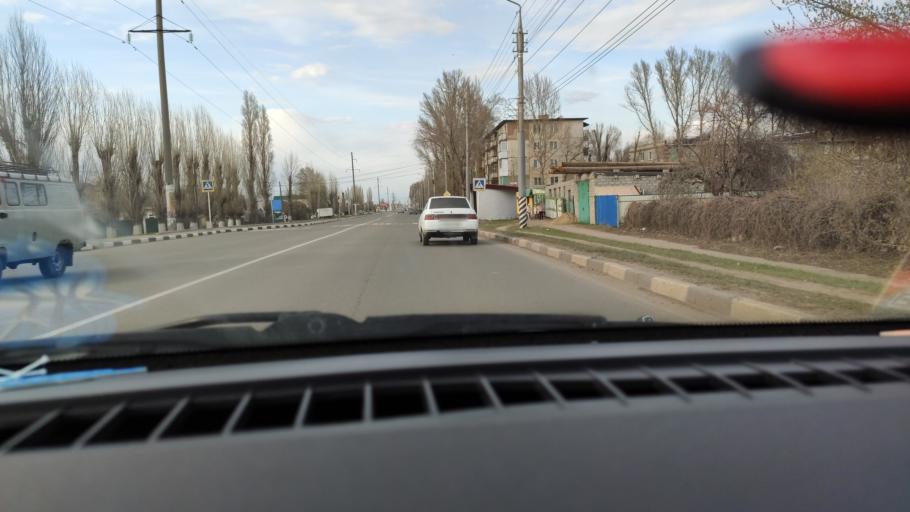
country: RU
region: Saratov
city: Privolzhskiy
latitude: 51.4064
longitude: 46.0395
